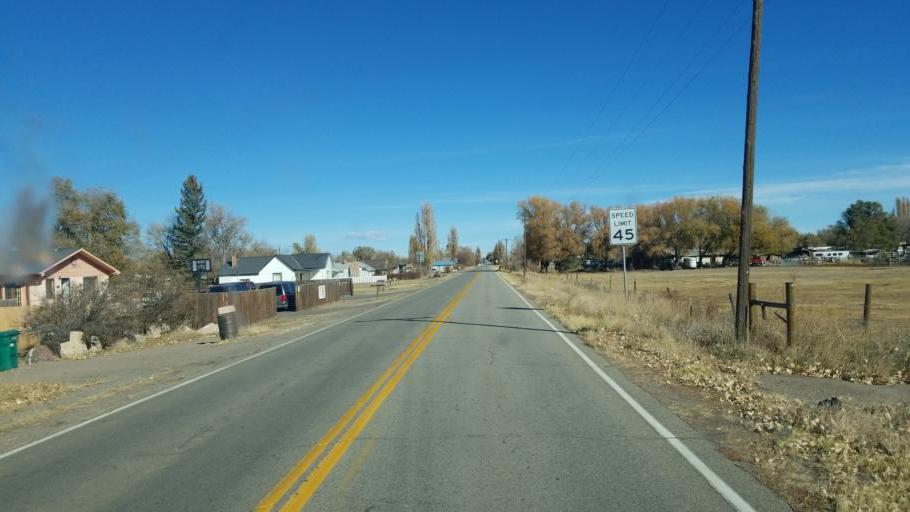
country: US
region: Colorado
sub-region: Rio Grande County
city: Monte Vista
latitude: 37.5692
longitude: -106.1495
